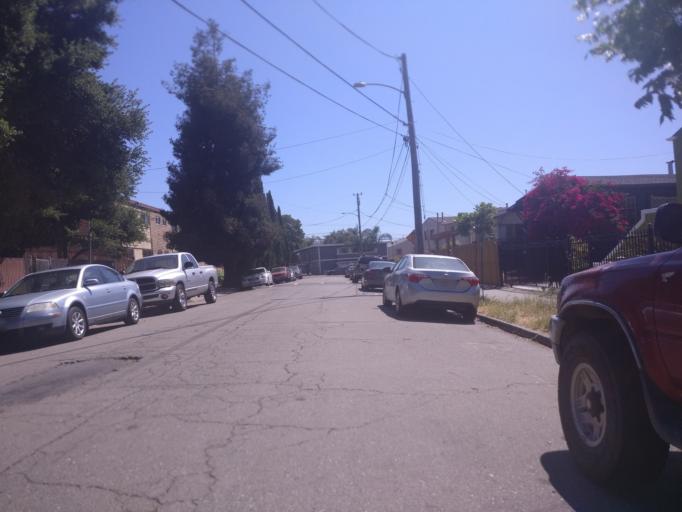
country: US
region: California
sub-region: Alameda County
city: Piedmont
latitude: 37.7949
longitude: -122.2168
